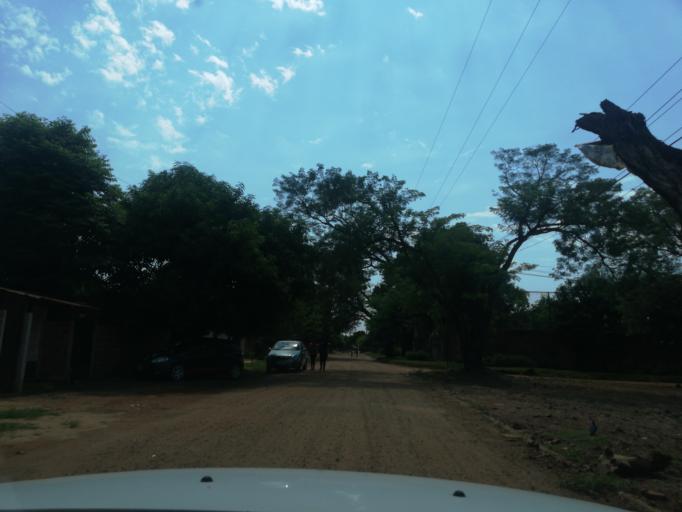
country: AR
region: Misiones
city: Garupa
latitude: -27.4388
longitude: -55.8853
